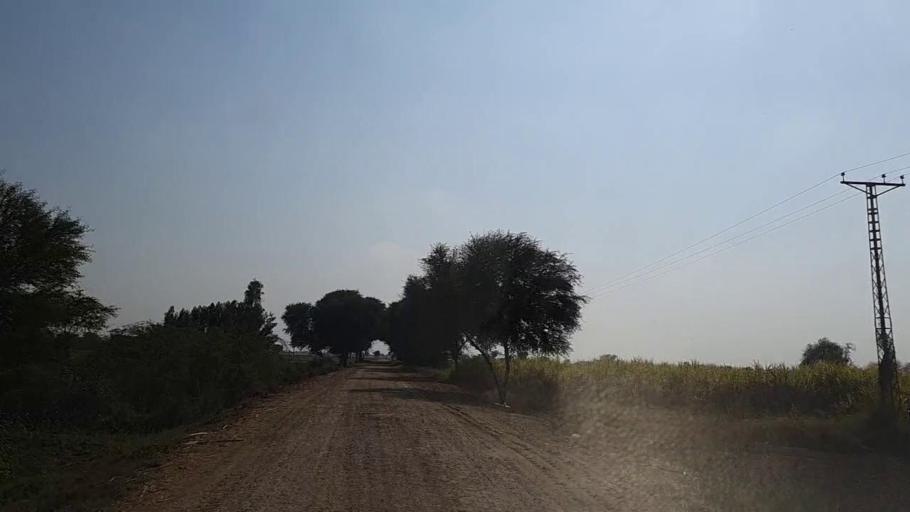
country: PK
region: Sindh
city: Daur
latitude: 26.4497
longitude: 68.2347
